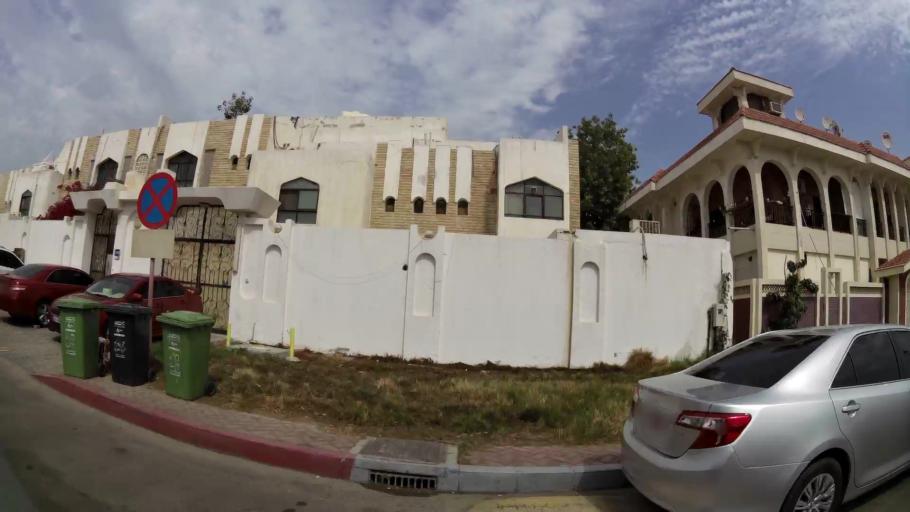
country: AE
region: Abu Dhabi
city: Abu Dhabi
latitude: 24.4621
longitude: 54.3665
